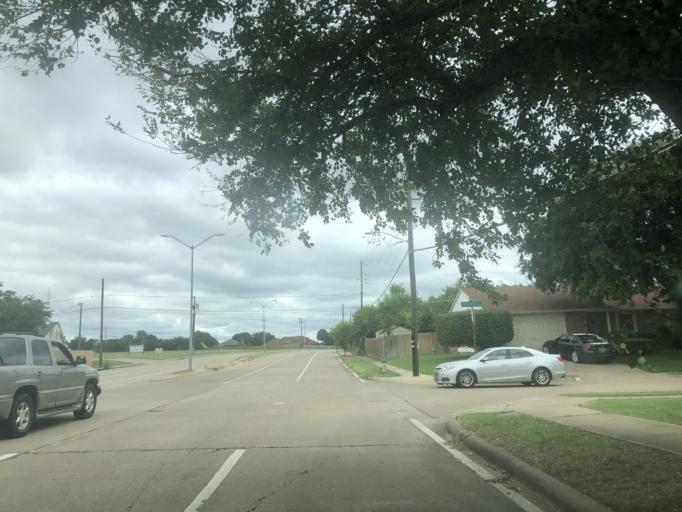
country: US
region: Texas
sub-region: Dallas County
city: Duncanville
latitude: 32.6443
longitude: -96.9524
